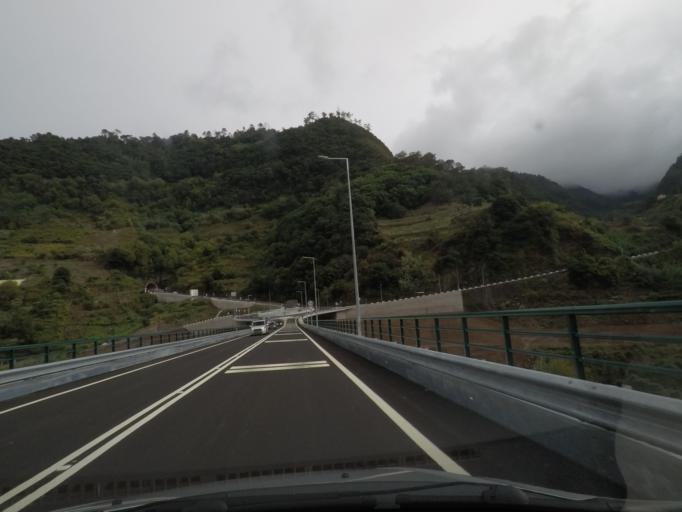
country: PT
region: Madeira
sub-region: Santana
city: Santana
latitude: 32.8162
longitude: -16.9020
